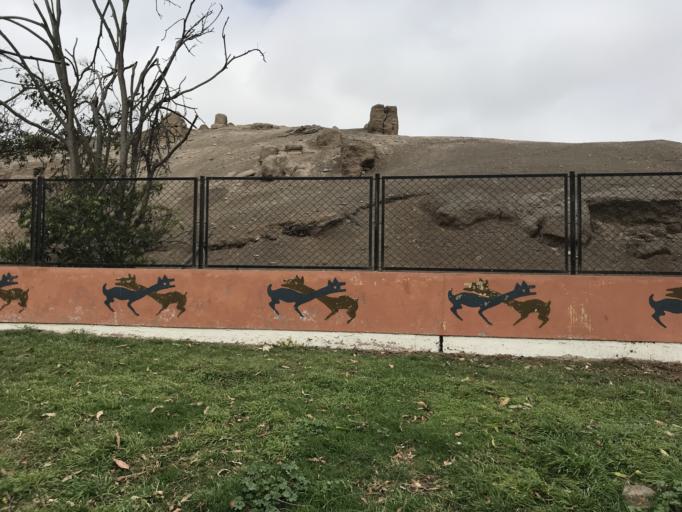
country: PE
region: Callao
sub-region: Callao
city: Callao
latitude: -12.0712
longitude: -77.0837
